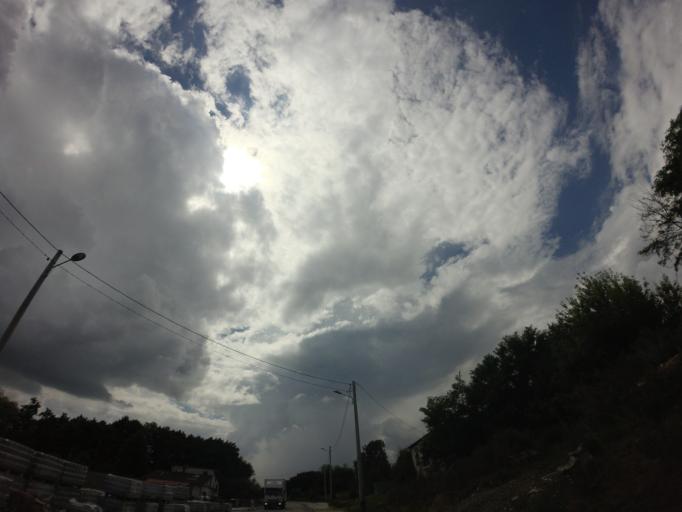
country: PL
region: Swietokrzyskie
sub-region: Powiat opatowski
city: Tarlow
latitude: 51.0360
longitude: 21.6908
